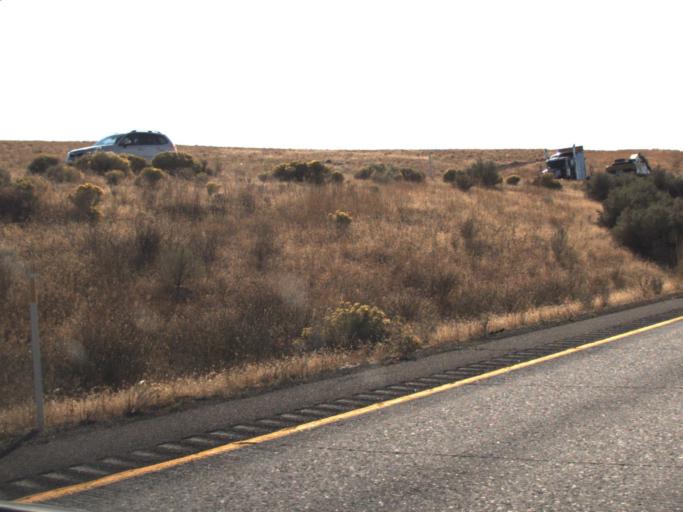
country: US
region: Oregon
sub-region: Umatilla County
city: Umatilla
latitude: 45.9838
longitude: -119.3163
